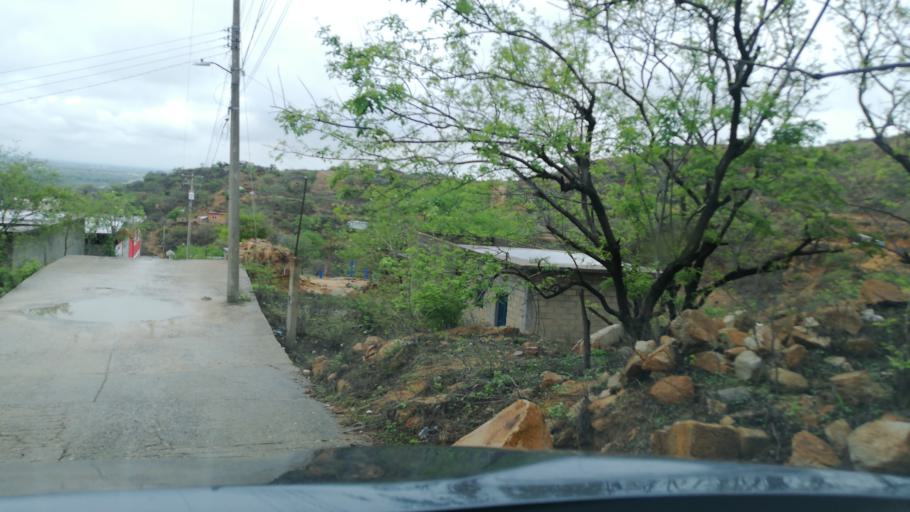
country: MX
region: Oaxaca
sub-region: Salina Cruz
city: Salina Cruz
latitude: 16.1805
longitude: -95.1839
